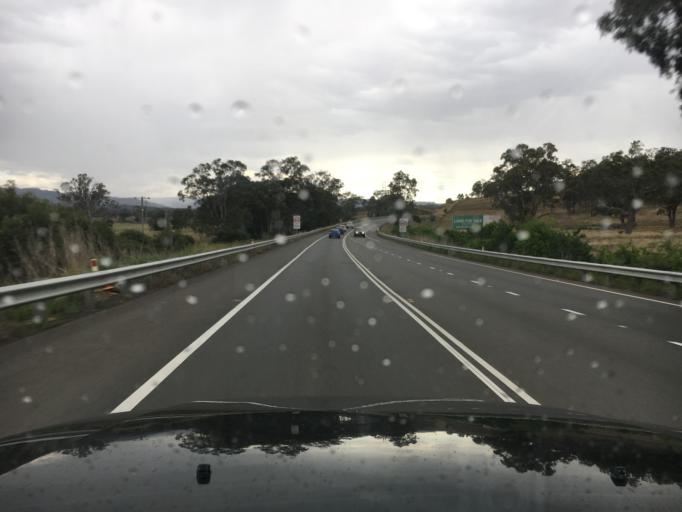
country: AU
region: New South Wales
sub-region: Muswellbrook
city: Muswellbrook
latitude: -32.2850
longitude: 150.9214
